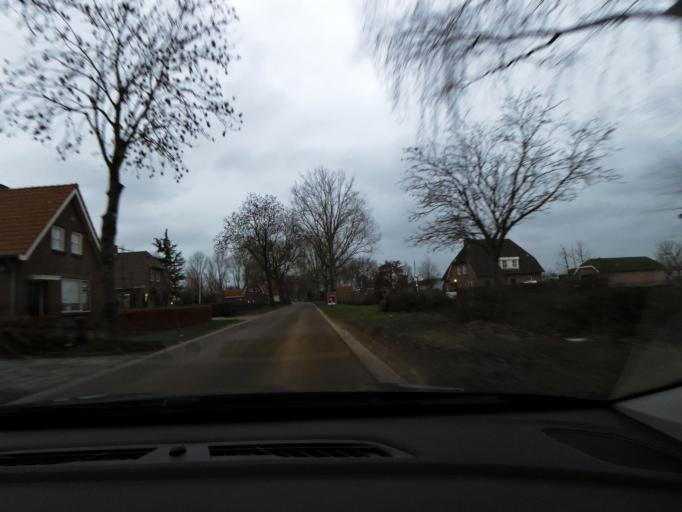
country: NL
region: North Brabant
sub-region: Gemeente Waalwijk
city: Waspik
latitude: 51.6865
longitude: 4.9841
